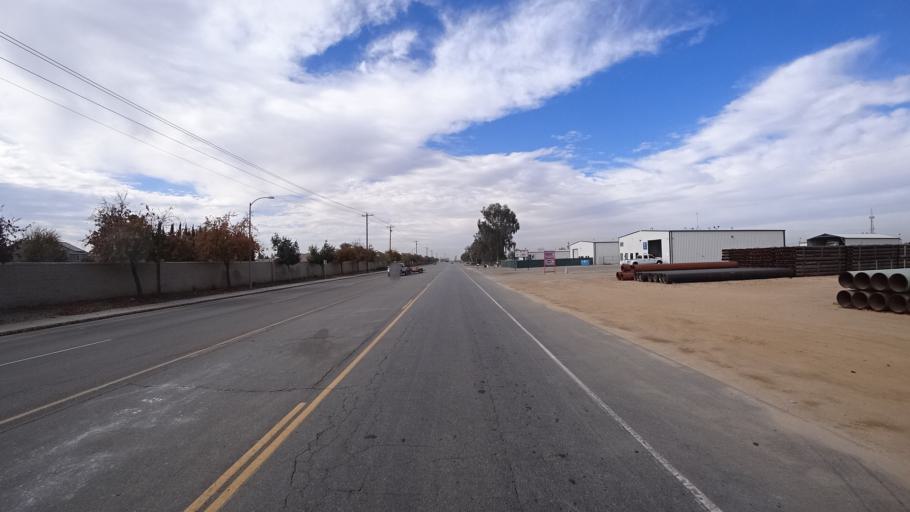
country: US
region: California
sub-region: Kern County
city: Rosedale
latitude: 35.4270
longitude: -119.1397
